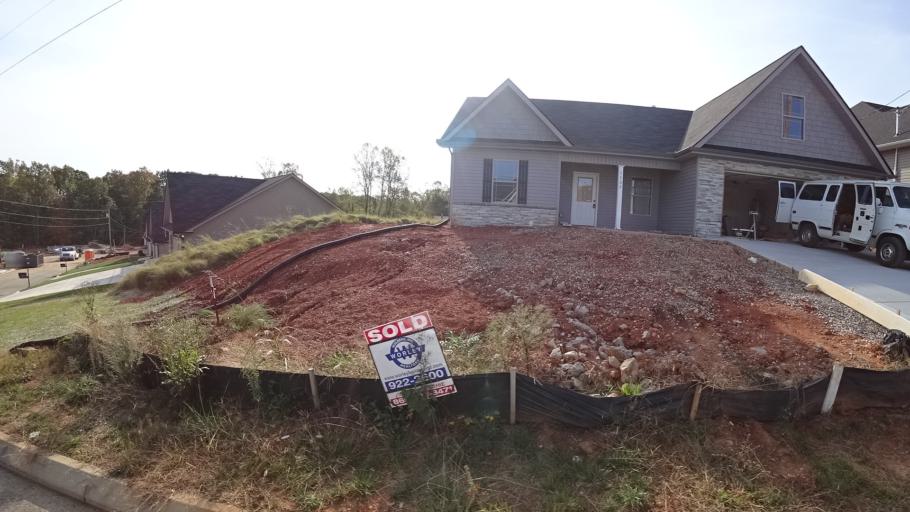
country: US
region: Tennessee
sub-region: Knox County
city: Farragut
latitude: 35.9090
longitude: -84.1763
